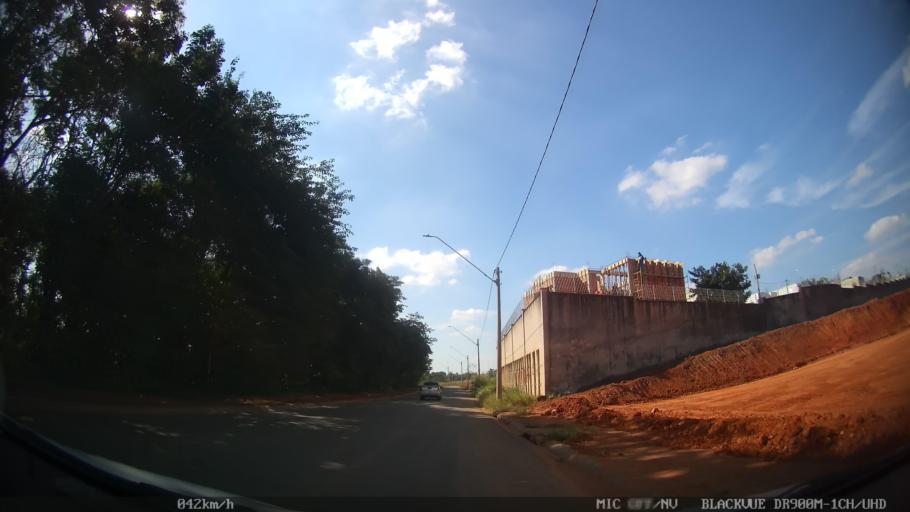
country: BR
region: Sao Paulo
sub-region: Hortolandia
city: Hortolandia
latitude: -22.8644
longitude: -47.2368
